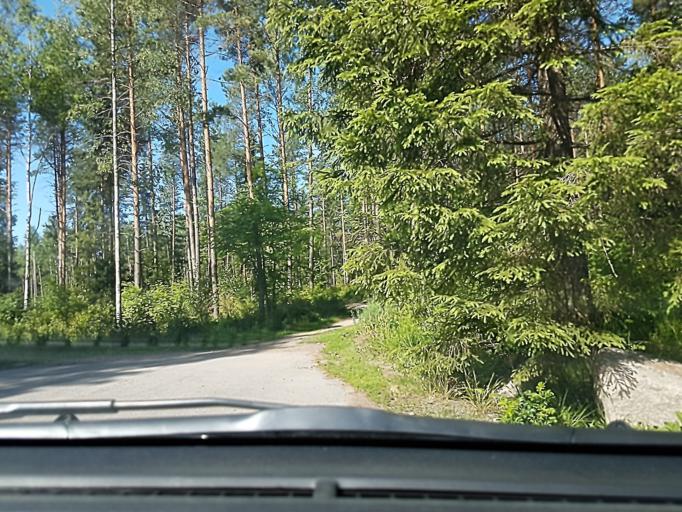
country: FI
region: Uusimaa
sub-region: Helsinki
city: Vantaa
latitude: 60.3366
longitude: 25.0541
